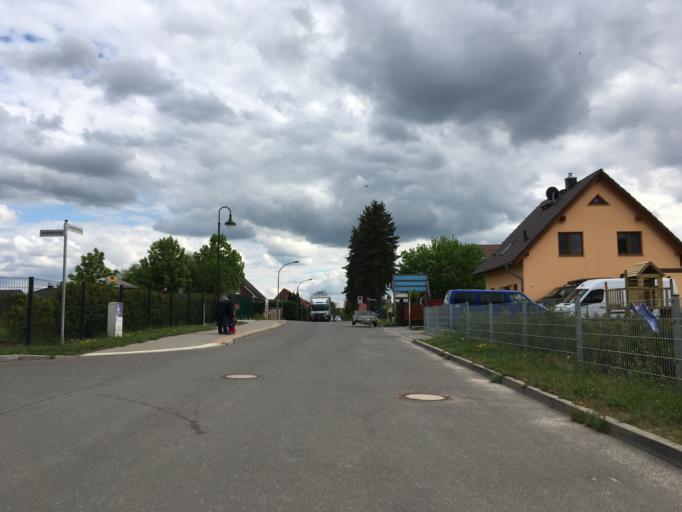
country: DE
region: Brandenburg
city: Bernau bei Berlin
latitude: 52.7005
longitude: 13.5944
